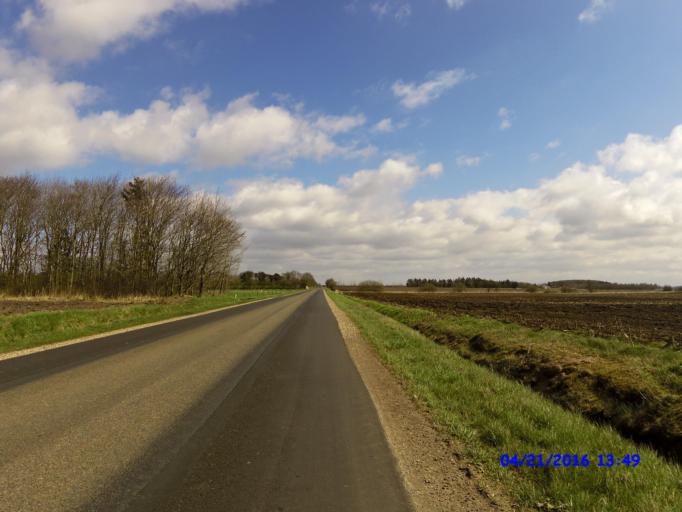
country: DK
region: South Denmark
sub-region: Haderslev Kommune
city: Gram
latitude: 55.2450
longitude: 8.9923
